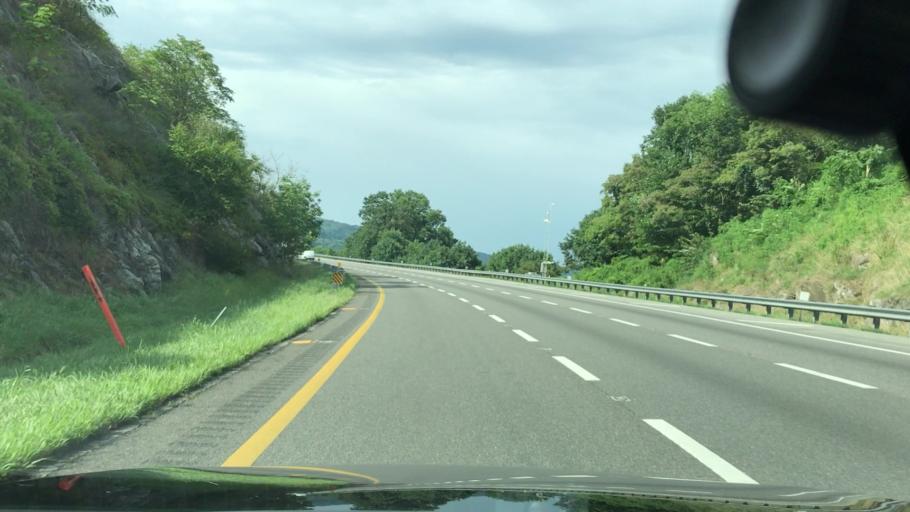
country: US
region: Virginia
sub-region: Carroll County
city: Cana
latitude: 36.6031
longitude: -80.7358
